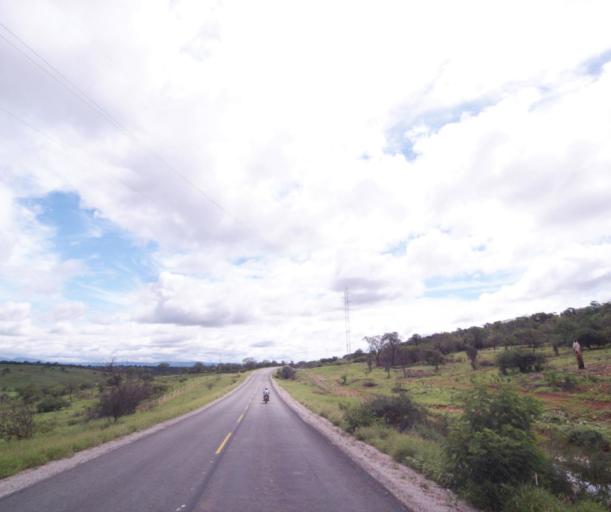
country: BR
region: Bahia
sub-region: Brumado
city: Brumado
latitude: -14.1526
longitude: -41.5110
